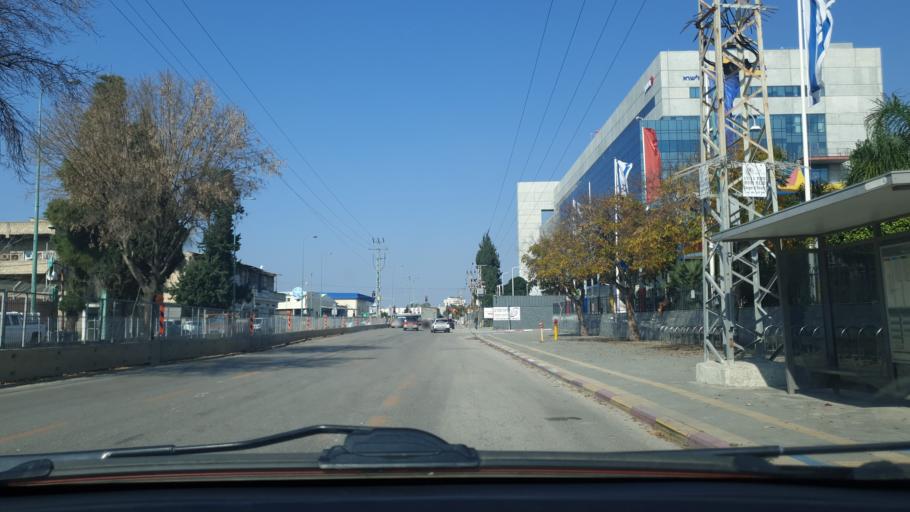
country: IL
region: Tel Aviv
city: Azor
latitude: 32.0104
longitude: 34.8081
